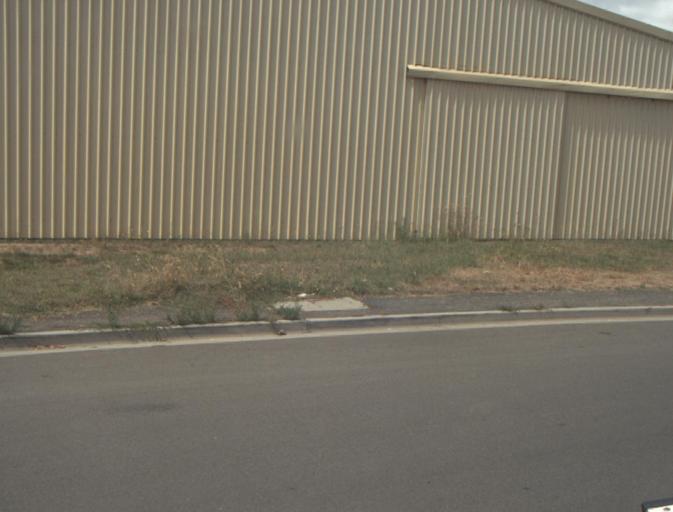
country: AU
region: Tasmania
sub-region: Launceston
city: Launceston
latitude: -41.4211
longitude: 147.1417
